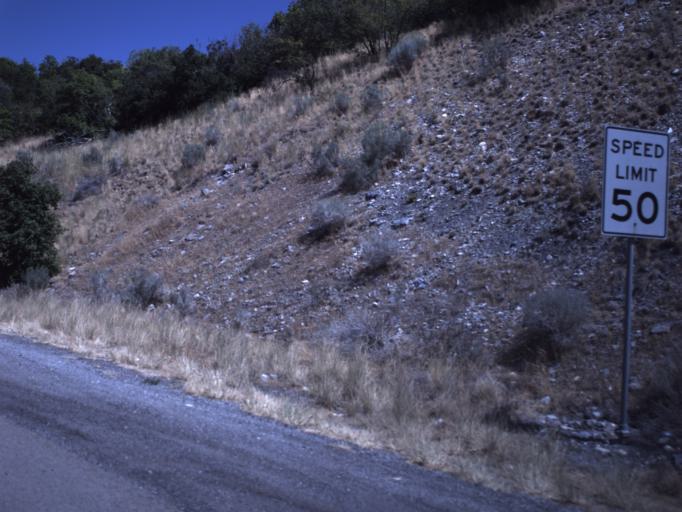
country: US
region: Utah
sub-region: Utah County
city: Orem
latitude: 40.3178
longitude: -111.6500
